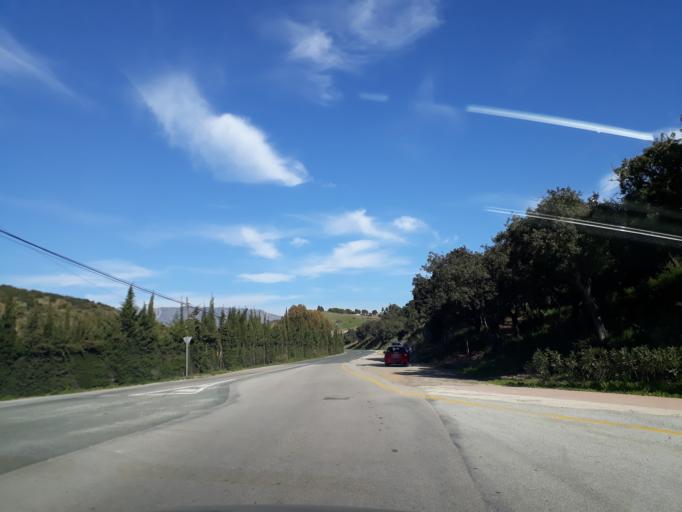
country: ES
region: Andalusia
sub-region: Provincia de Malaga
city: Fuengirola
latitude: 36.5149
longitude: -4.6863
